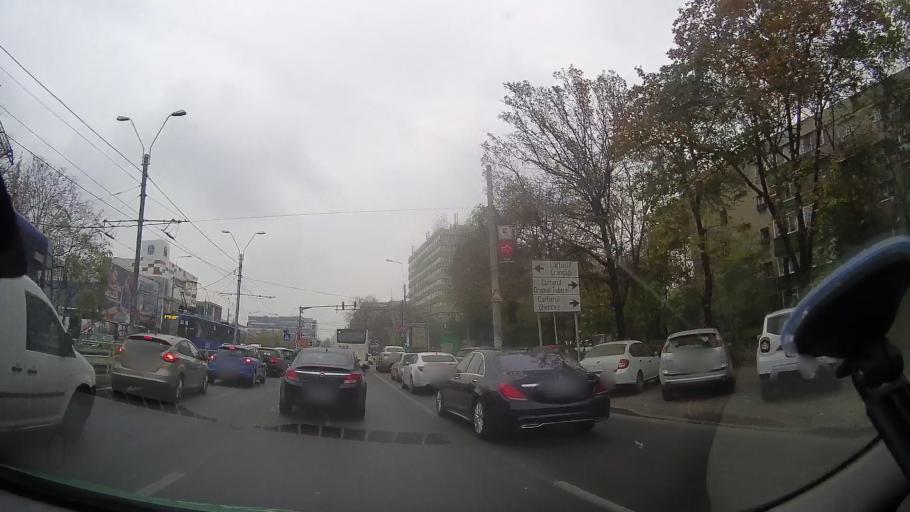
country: RO
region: Ilfov
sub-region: Comuna Chiajna
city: Rosu
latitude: 44.4272
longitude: 26.0327
